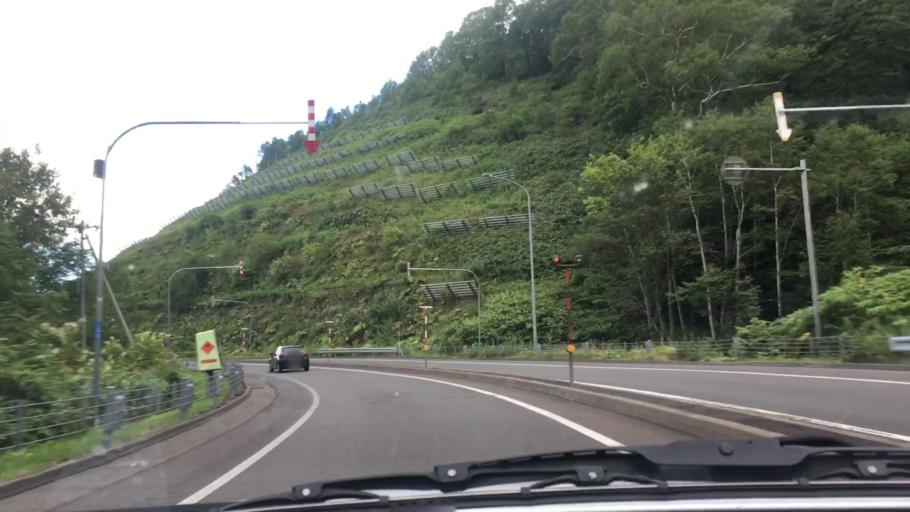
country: JP
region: Hokkaido
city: Shimo-furano
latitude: 43.1500
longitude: 142.7733
